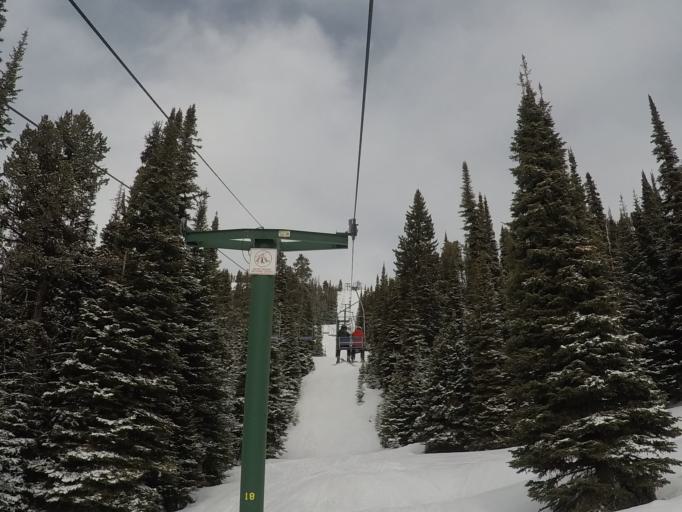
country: US
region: Montana
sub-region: Meagher County
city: White Sulphur Springs
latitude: 46.8343
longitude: -110.7107
